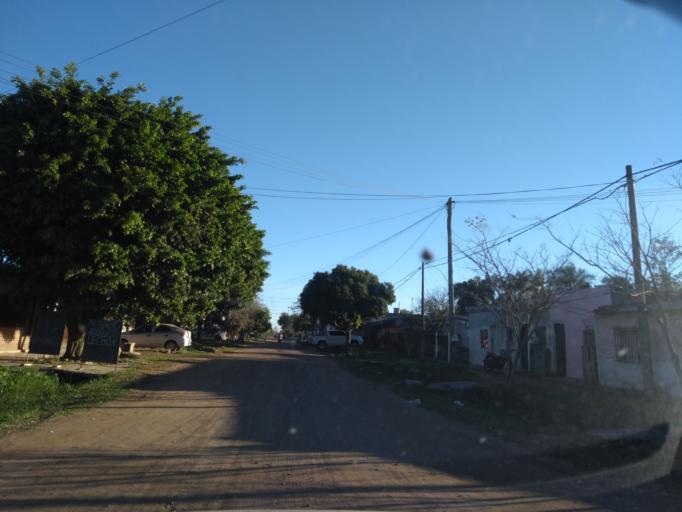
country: AR
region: Chaco
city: Barranqueras
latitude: -27.4877
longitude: -58.9327
